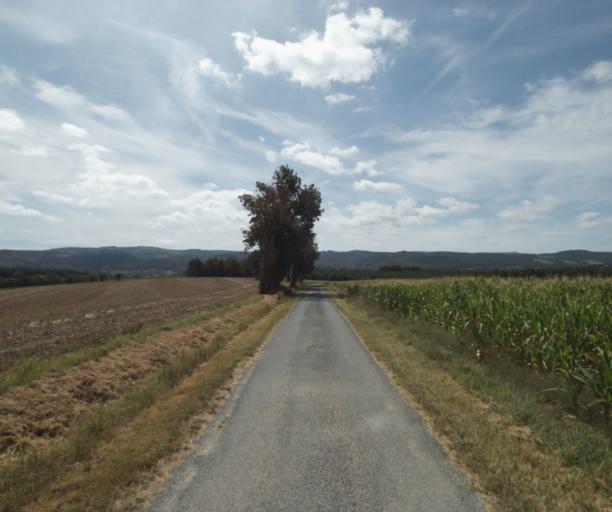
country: FR
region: Midi-Pyrenees
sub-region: Departement du Tarn
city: Dourgne
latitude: 43.4922
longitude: 2.0961
